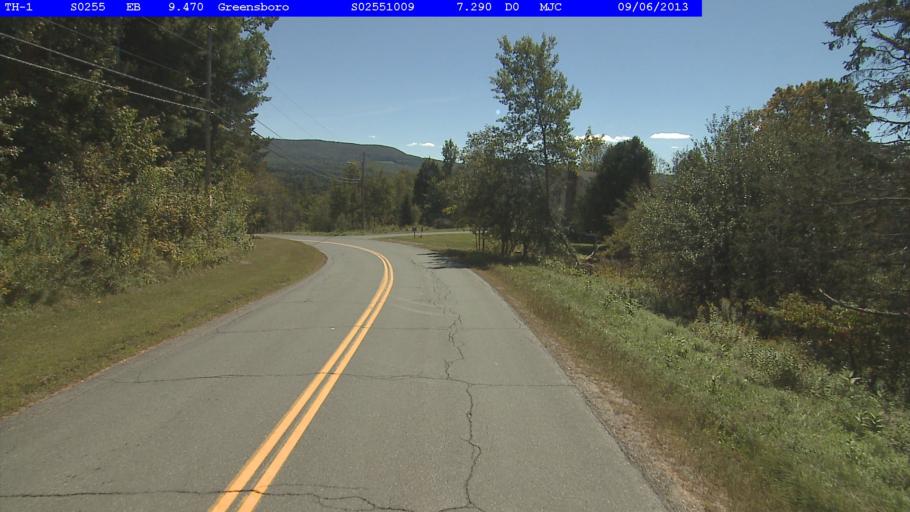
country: US
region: Vermont
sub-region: Caledonia County
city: Hardwick
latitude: 44.5509
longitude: -72.2705
